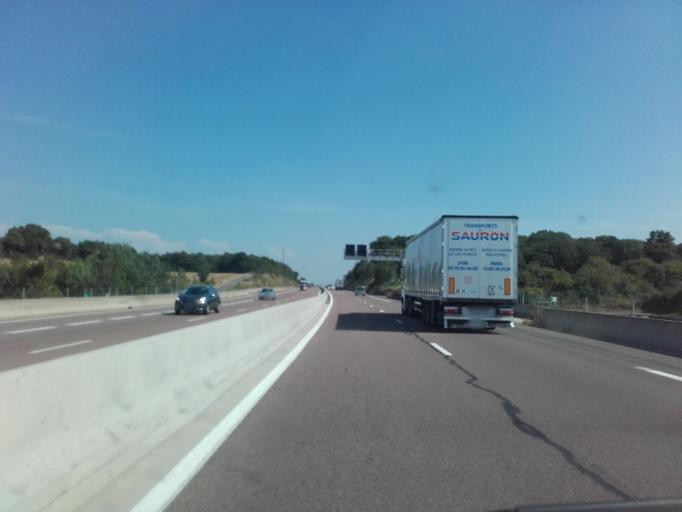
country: FR
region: Bourgogne
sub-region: Departement de la Cote-d'Or
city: Savigny-les-Beaune
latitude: 47.0892
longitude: 4.7541
